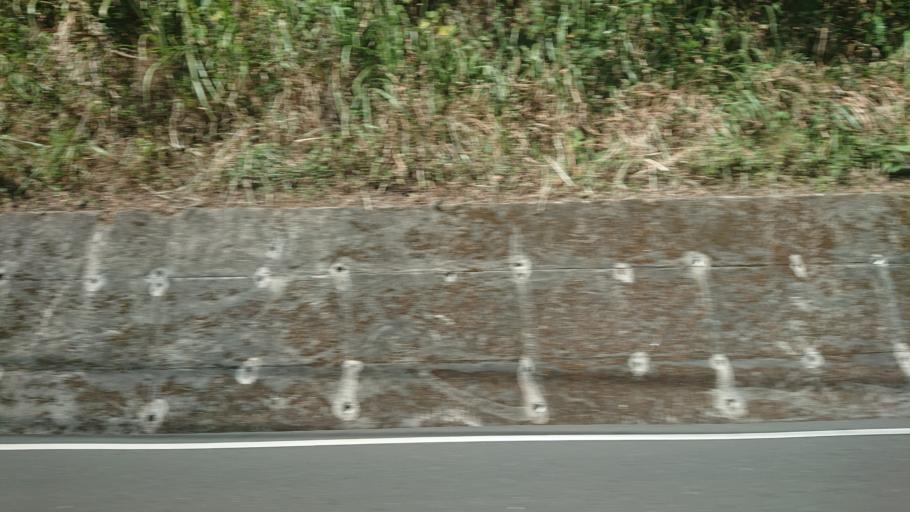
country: TW
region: Taiwan
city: Lugu
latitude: 23.4687
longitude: 120.7306
